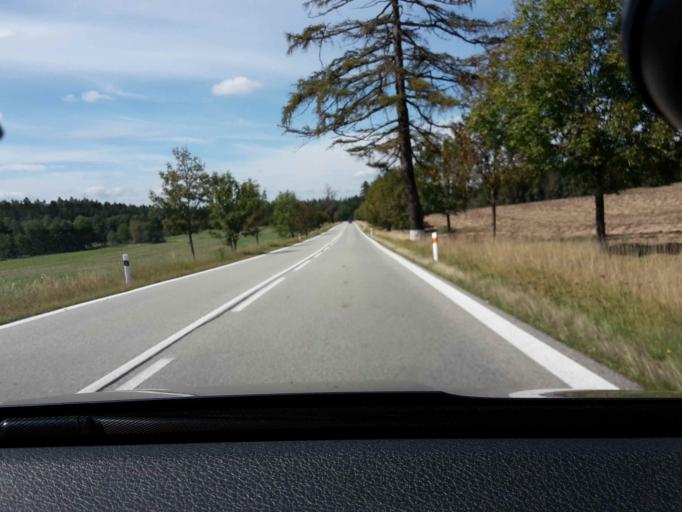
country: CZ
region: Jihocesky
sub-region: Okres Jindrichuv Hradec
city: Jindrichuv Hradec
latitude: 49.1630
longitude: 14.9362
